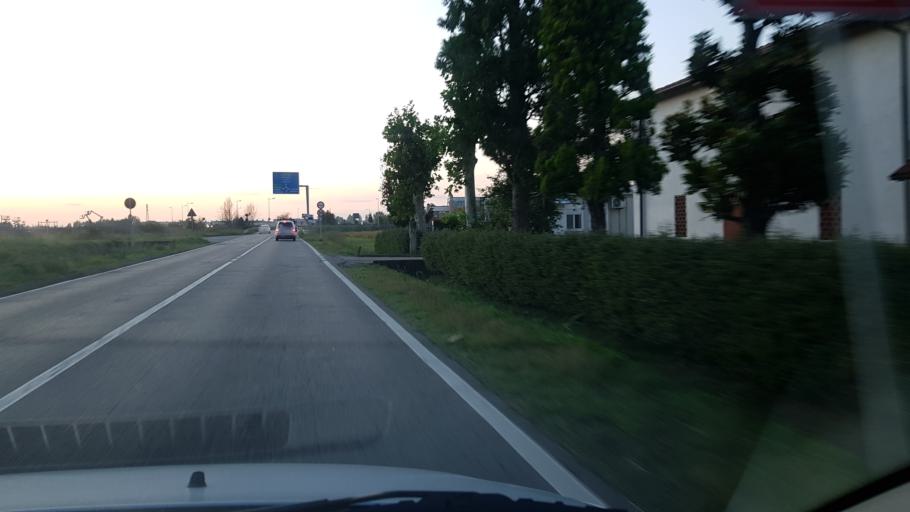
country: IT
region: Emilia-Romagna
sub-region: Provincia di Modena
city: Cavezzo
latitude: 44.8206
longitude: 11.0470
